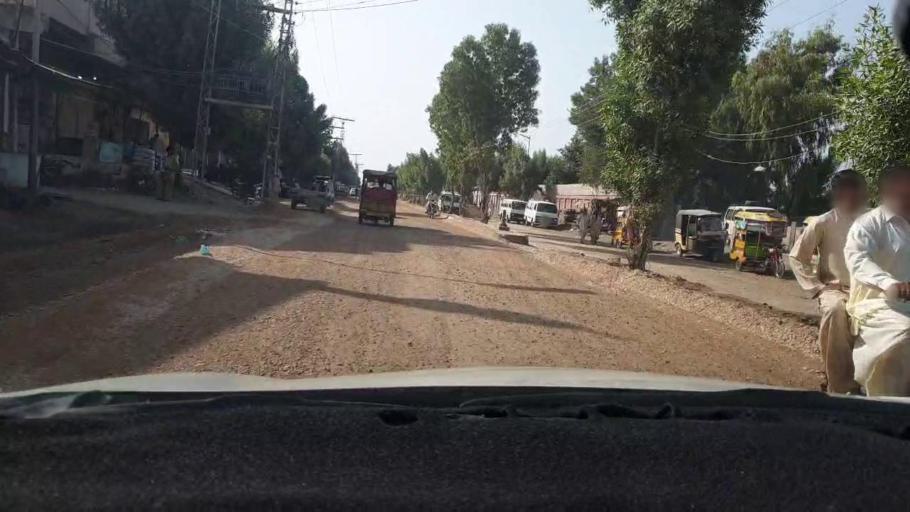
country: PK
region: Sindh
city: Sanghar
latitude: 26.0424
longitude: 68.9498
